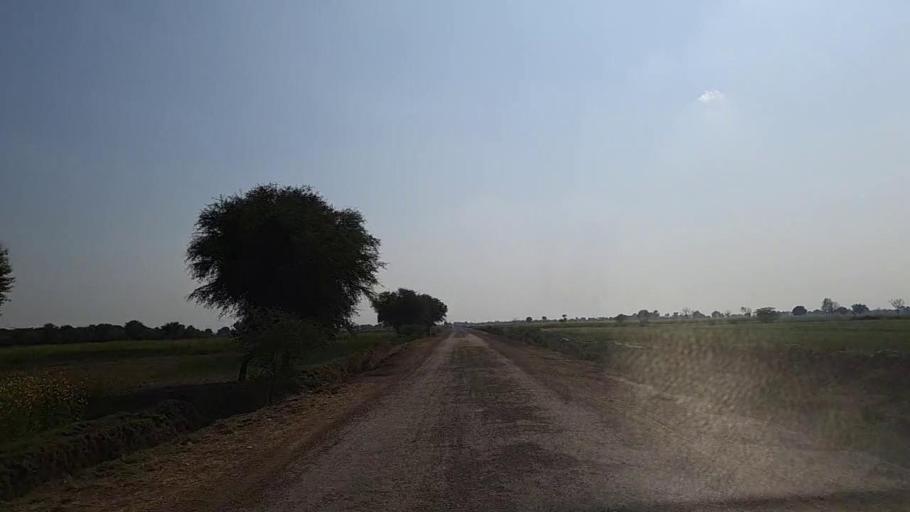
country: PK
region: Sindh
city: Jam Sahib
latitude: 26.2590
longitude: 68.5670
